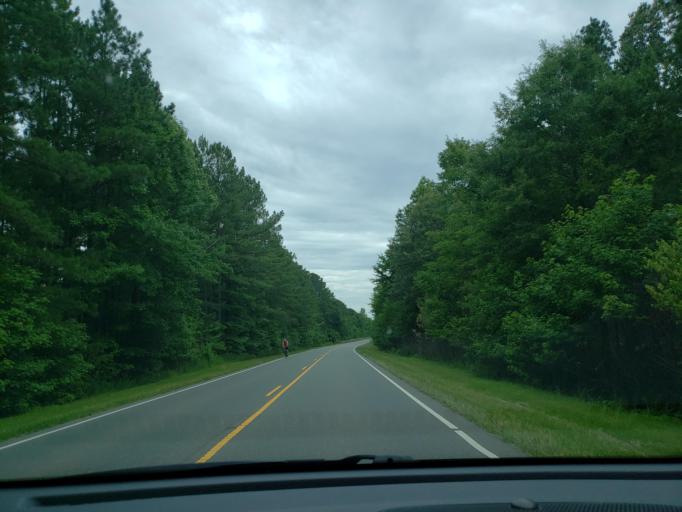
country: US
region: North Carolina
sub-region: Chatham County
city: Fearrington Village
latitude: 35.7836
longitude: -79.0087
